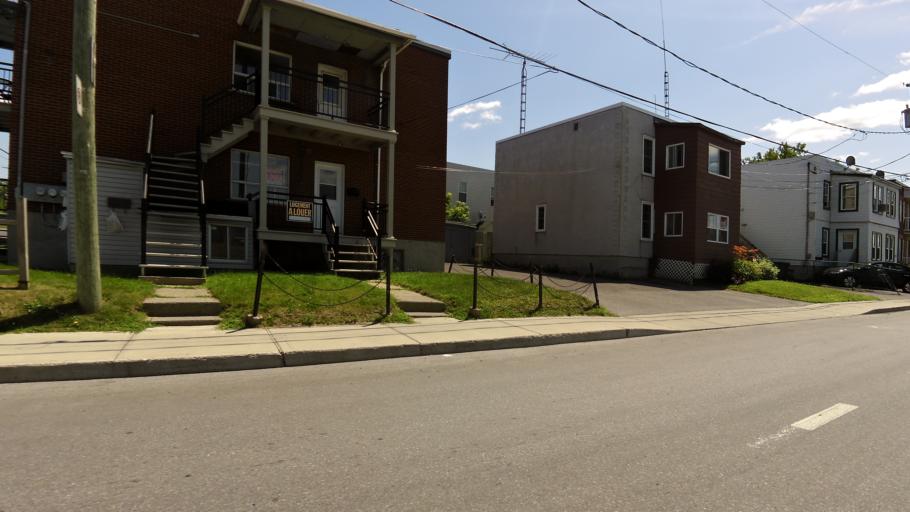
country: CA
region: Quebec
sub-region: Monteregie
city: Saint-Jean-sur-Richelieu
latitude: 45.3090
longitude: -73.2647
